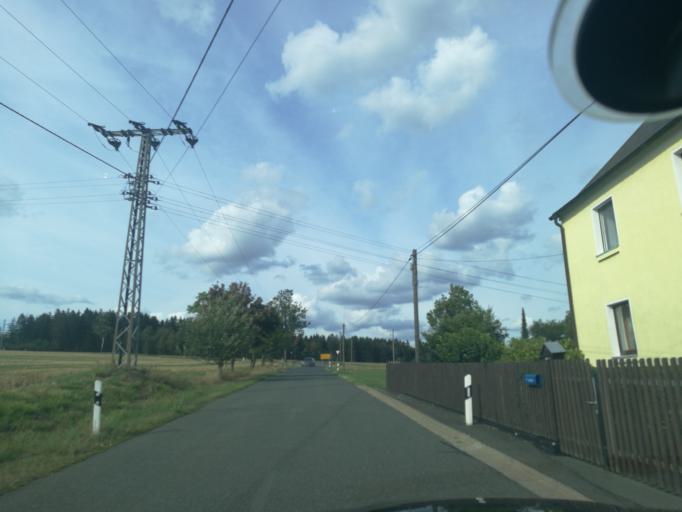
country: DE
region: Saxony
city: Triebel
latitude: 50.3314
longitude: 12.1203
